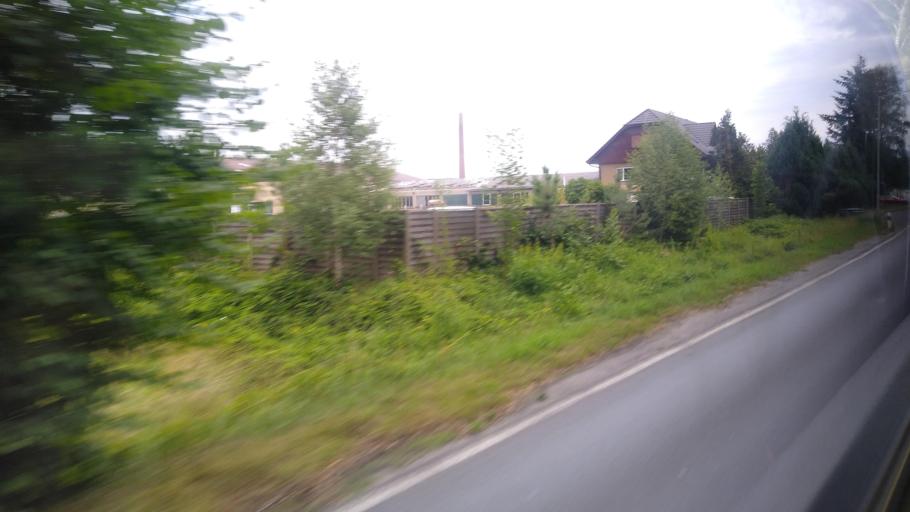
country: DE
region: North Rhine-Westphalia
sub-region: Regierungsbezirk Detmold
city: Hovelhof
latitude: 51.8275
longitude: 8.6409
